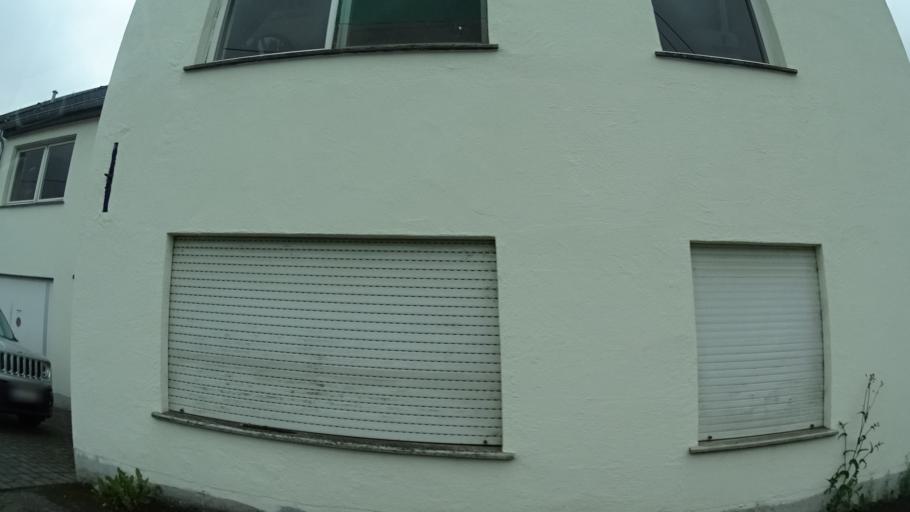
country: LU
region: Luxembourg
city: Eischen
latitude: 49.6491
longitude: 5.8696
